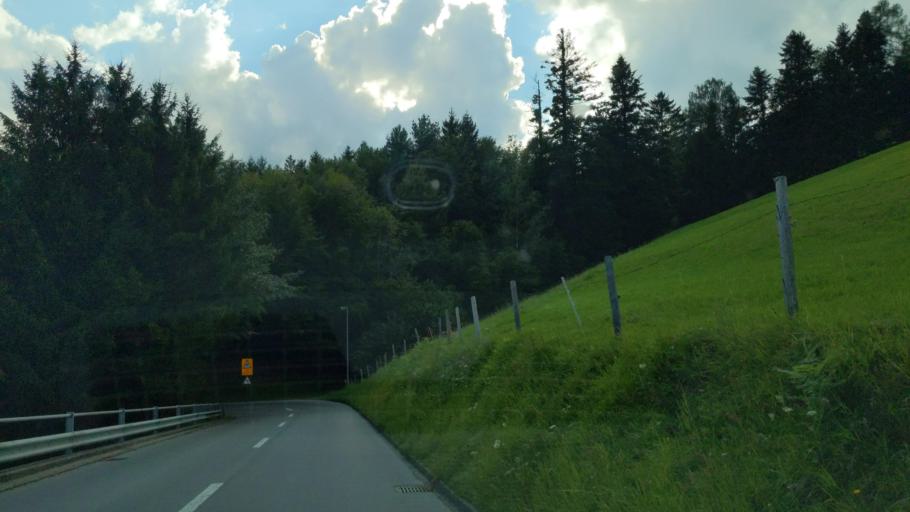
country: CH
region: Saint Gallen
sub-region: Wahlkreis Rheintal
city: Eichberg
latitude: 47.3434
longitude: 9.5123
